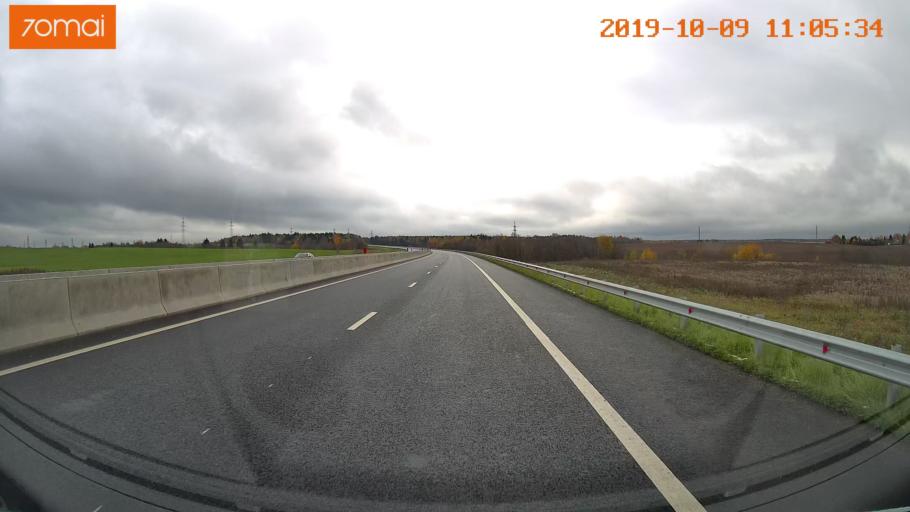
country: RU
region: Vologda
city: Molochnoye
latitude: 59.1983
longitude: 39.7581
